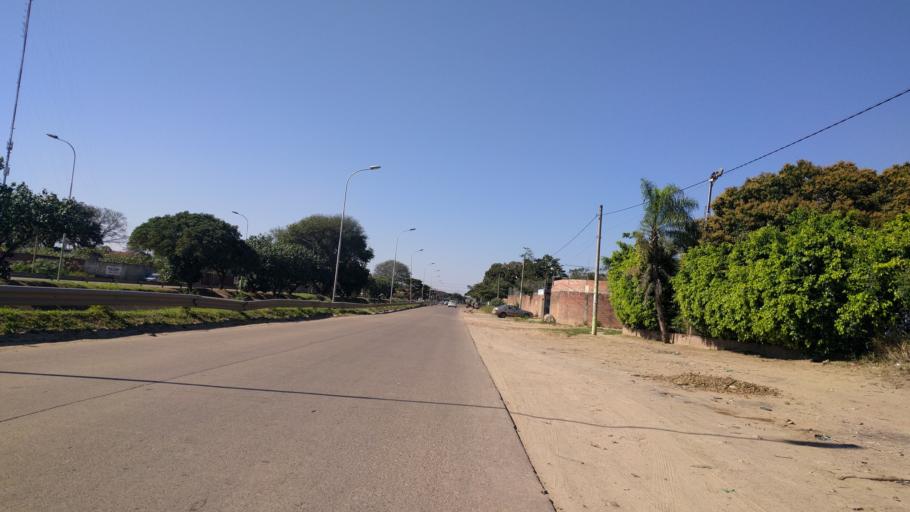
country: BO
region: Santa Cruz
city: Santa Cruz de la Sierra
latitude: -17.8204
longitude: -63.2227
